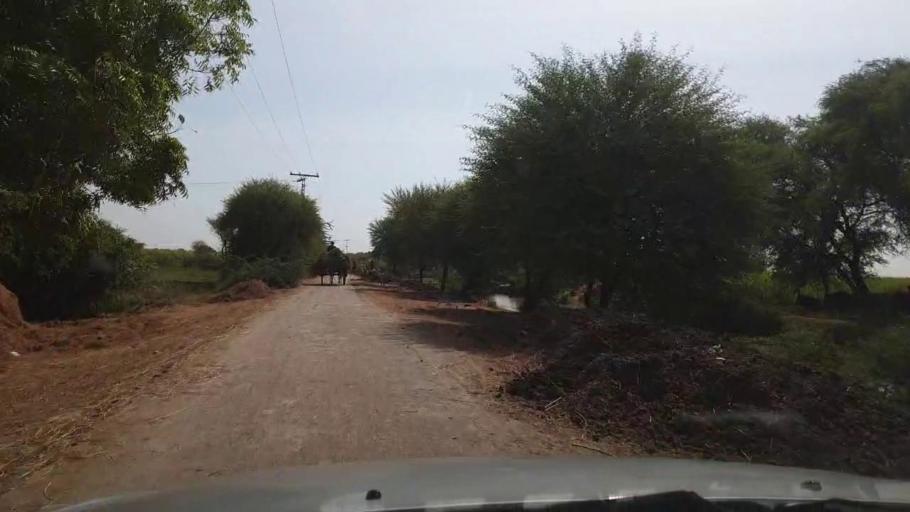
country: PK
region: Sindh
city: Tando Muhammad Khan
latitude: 25.1469
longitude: 68.3960
